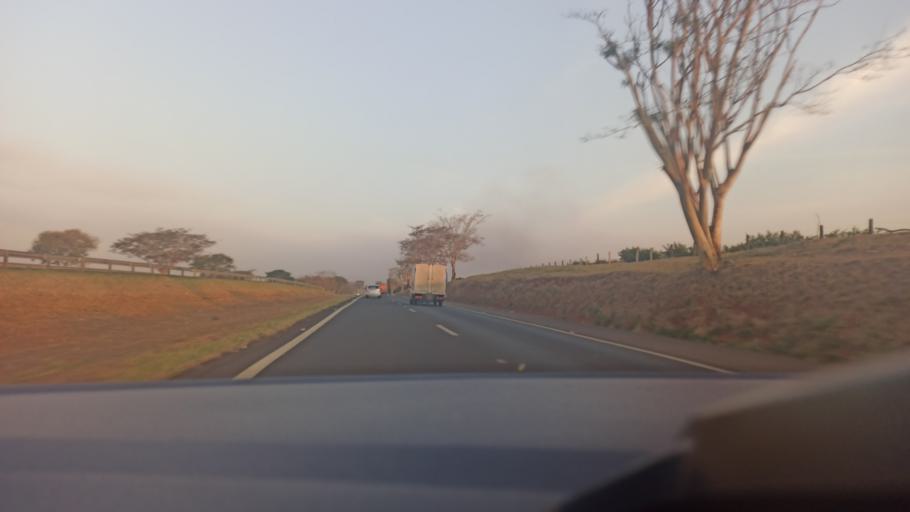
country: BR
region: Sao Paulo
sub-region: Taquaritinga
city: Taquaritinga
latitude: -21.4582
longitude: -48.6239
